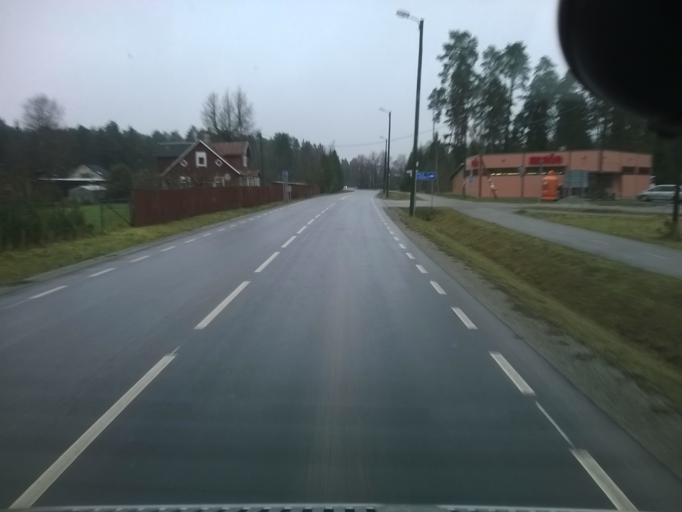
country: EE
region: Harju
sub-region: Saku vald
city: Saku
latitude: 59.2210
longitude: 24.6710
